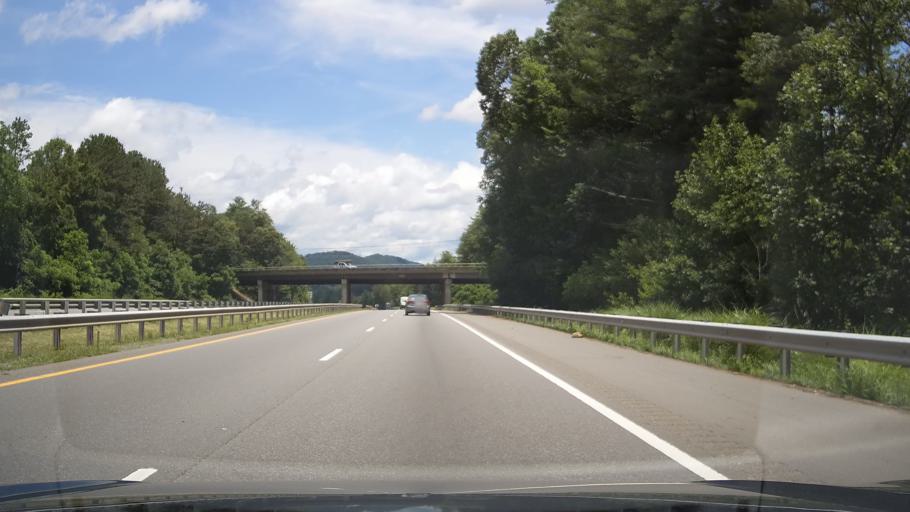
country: US
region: North Carolina
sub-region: Buncombe County
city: Weaverville
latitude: 35.7125
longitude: -82.5630
